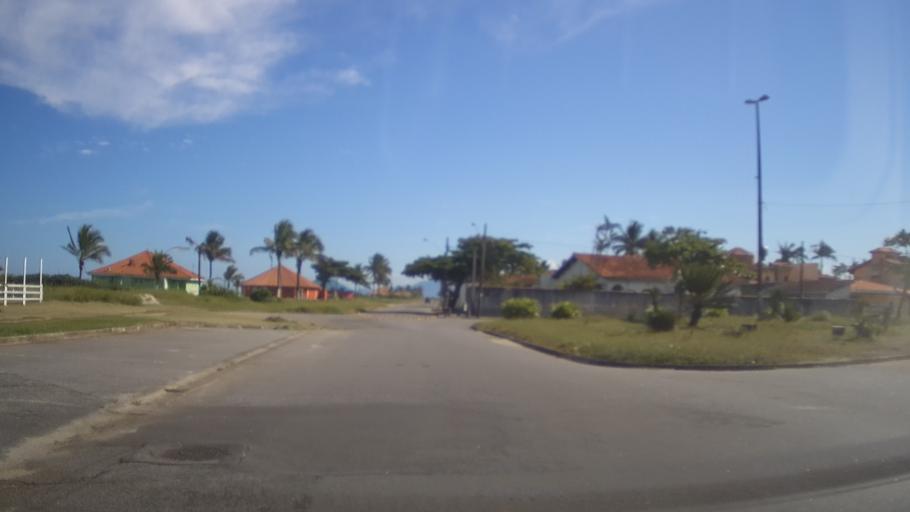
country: BR
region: Sao Paulo
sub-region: Itanhaem
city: Itanhaem
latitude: -24.2162
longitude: -46.8441
